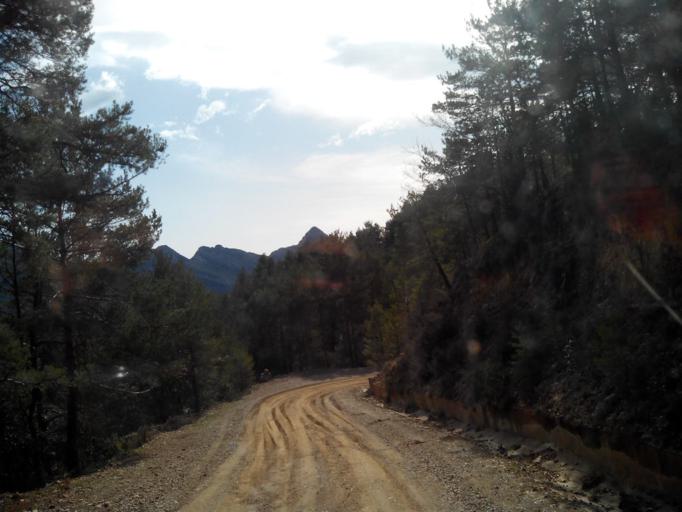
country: ES
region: Catalonia
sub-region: Provincia de Barcelona
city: Vilada
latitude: 42.1488
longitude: 1.9299
